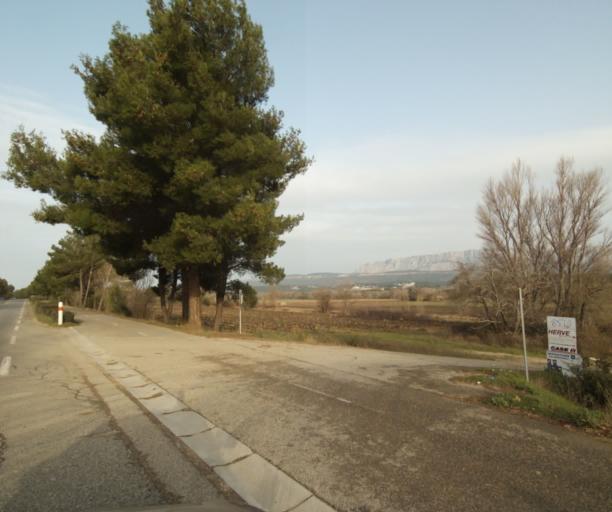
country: FR
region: Provence-Alpes-Cote d'Azur
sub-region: Departement des Bouches-du-Rhone
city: Peynier
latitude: 43.4601
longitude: 5.6424
